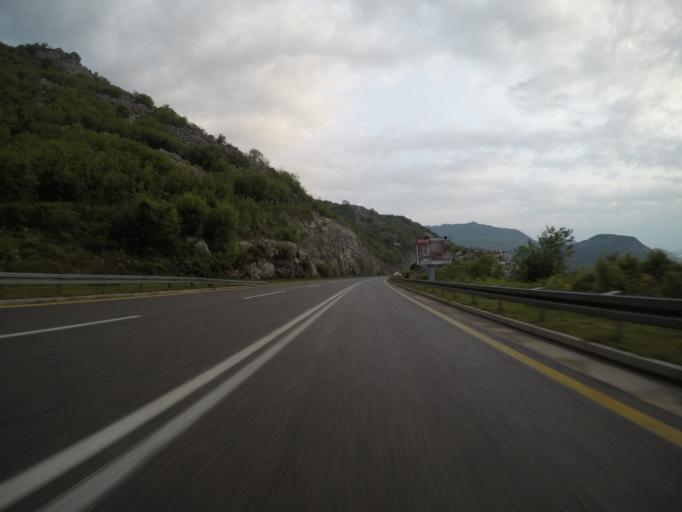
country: ME
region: Bar
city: Sutomore
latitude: 42.2100
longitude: 19.0483
